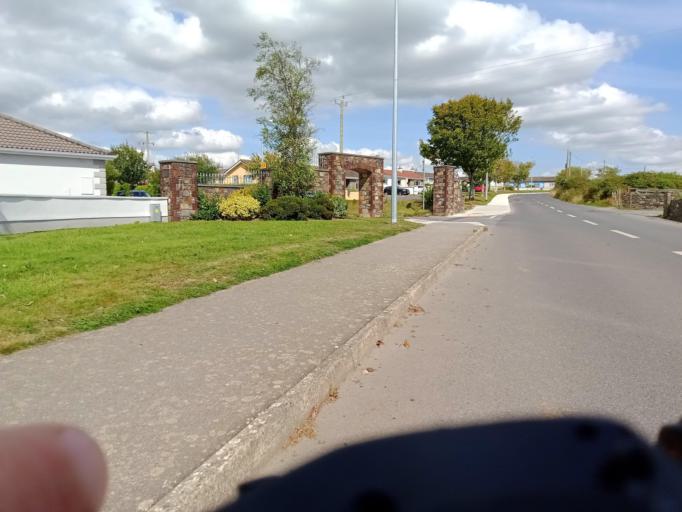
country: IE
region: Munster
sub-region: Waterford
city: Dungarvan
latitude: 52.1326
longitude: -7.4584
